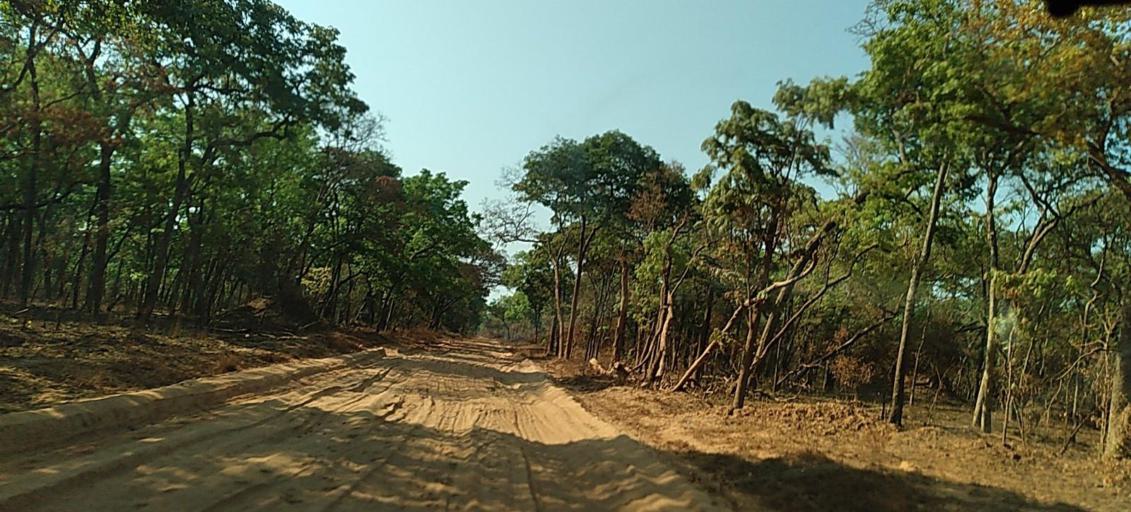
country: ZM
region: North-Western
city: Kasempa
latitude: -13.6780
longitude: 26.0217
